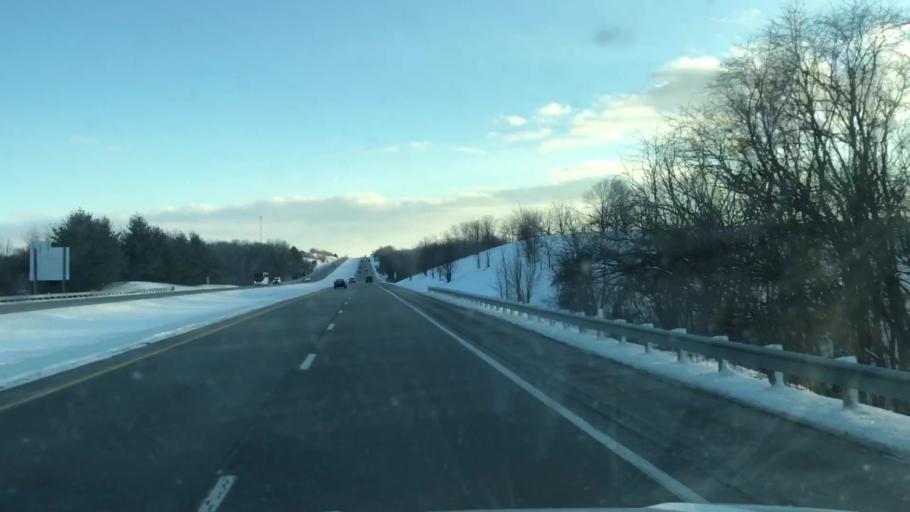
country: US
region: Missouri
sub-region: Andrew County
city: Country Club Village
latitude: 39.8419
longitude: -94.8055
